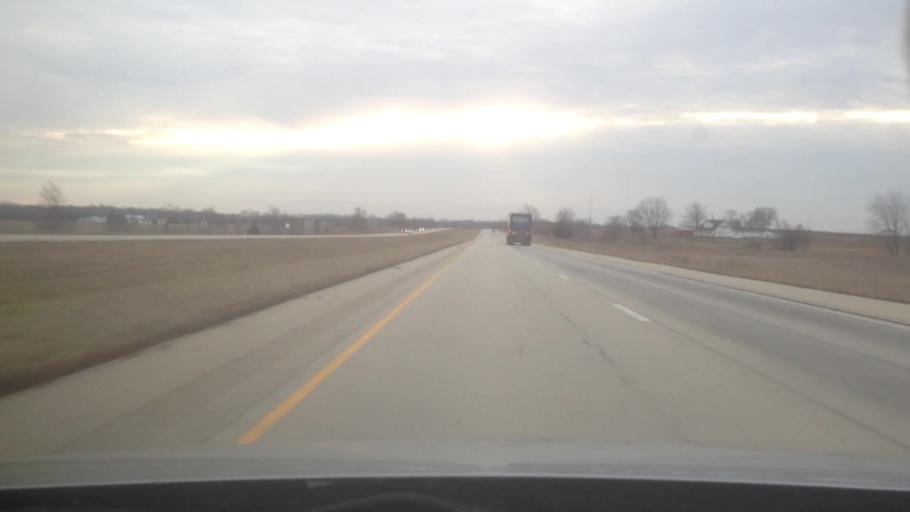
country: US
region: Illinois
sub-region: Macon County
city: Decatur
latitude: 39.7987
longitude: -89.0062
